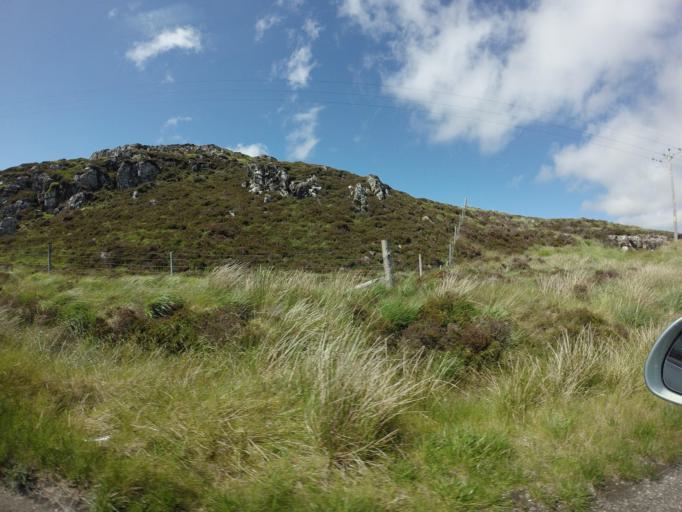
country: GB
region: Scotland
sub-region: Eilean Siar
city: Stornoway
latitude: 58.1411
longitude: -6.5078
